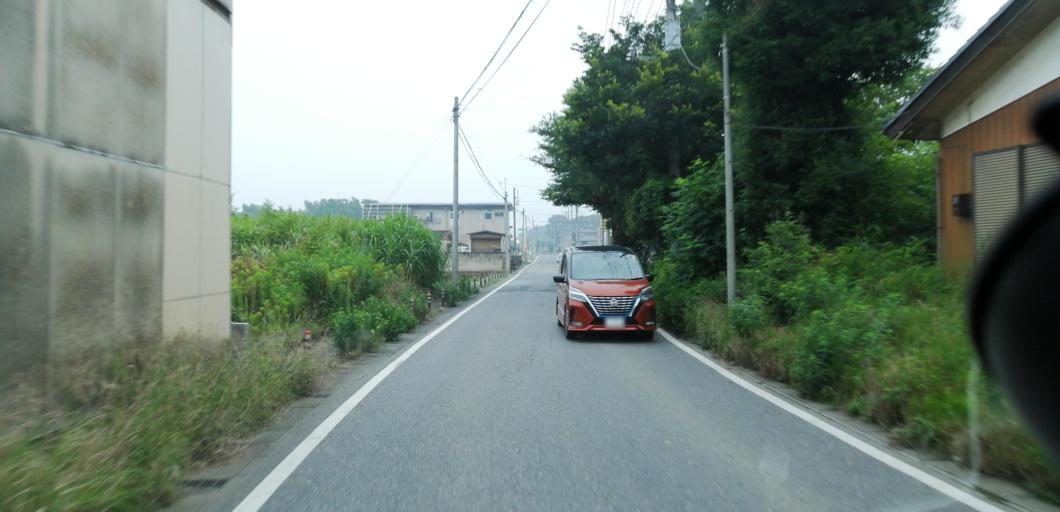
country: JP
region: Ibaraki
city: Iwai
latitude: 36.0140
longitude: 139.8471
